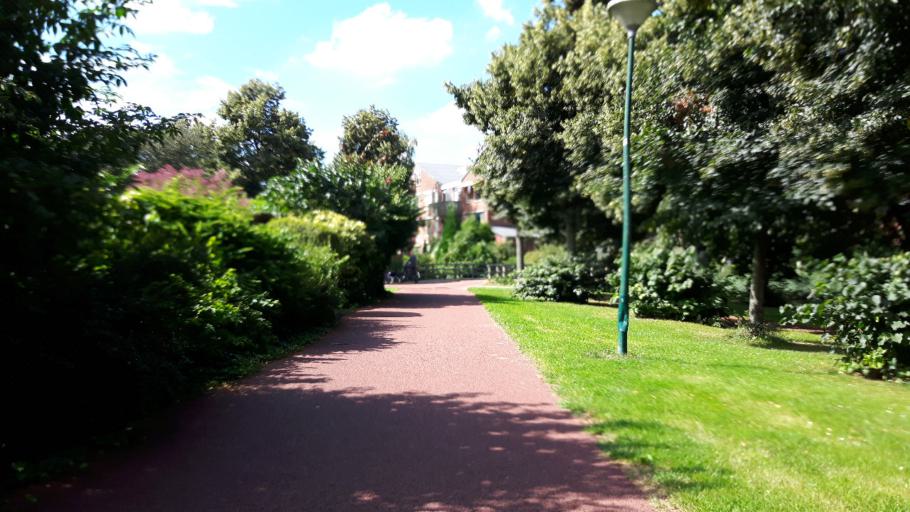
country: NL
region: Utrecht
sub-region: Stichtse Vecht
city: Spechtenkamp
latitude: 52.1406
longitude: 5.0166
